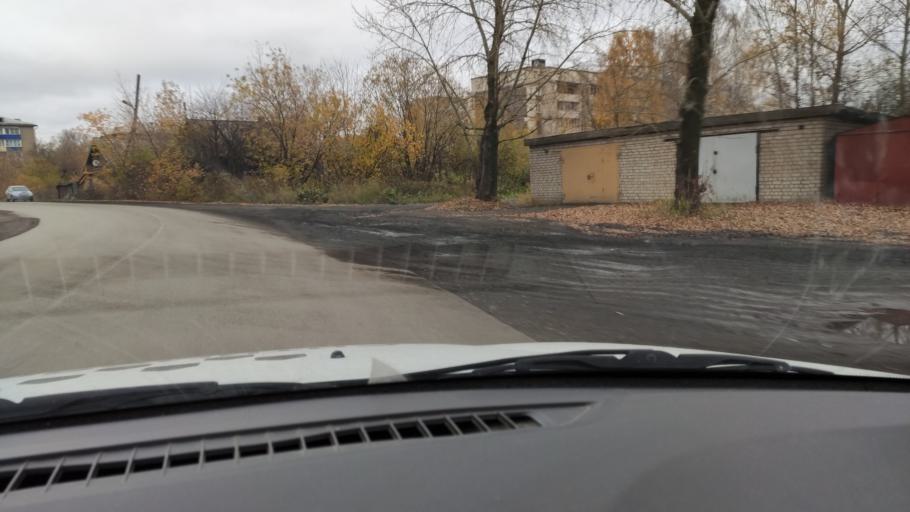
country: RU
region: Kirov
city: Slobodskoy
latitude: 58.7226
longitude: 50.1749
